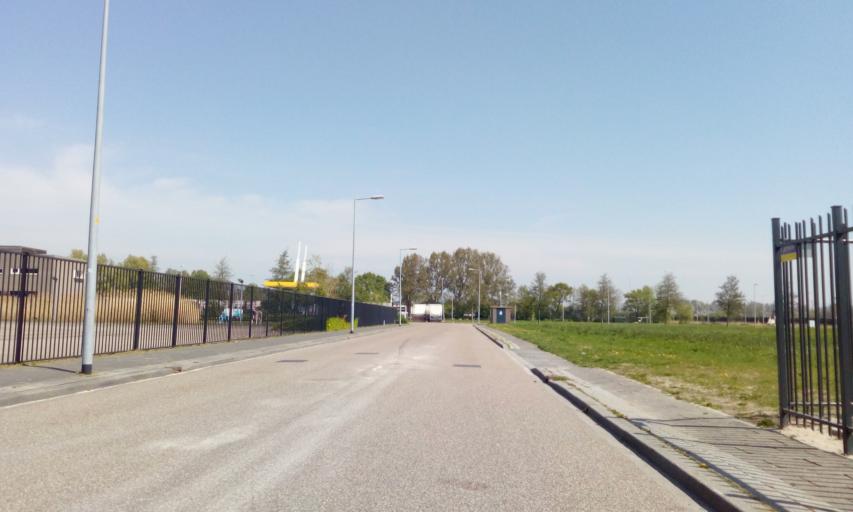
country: NL
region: South Holland
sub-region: Gemeente Kaag en Braassem
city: Oude Wetering
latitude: 52.2541
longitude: 4.6356
